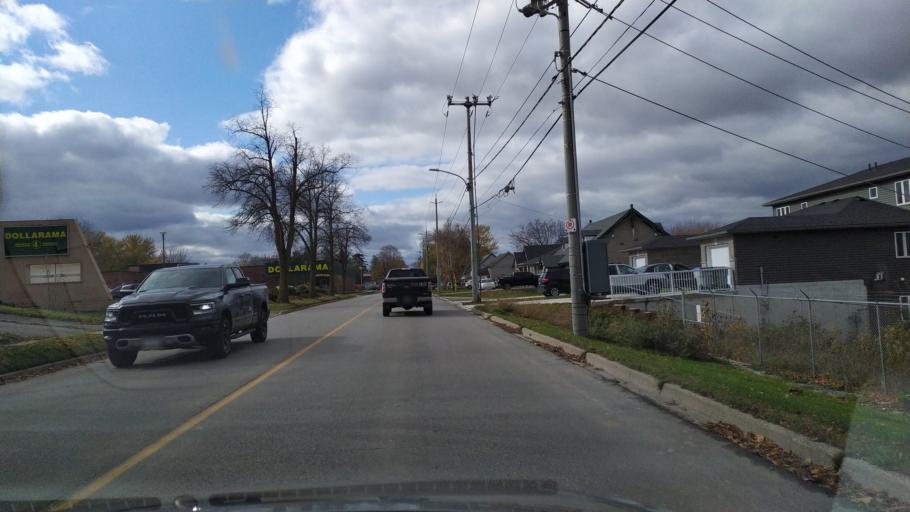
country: CA
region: Ontario
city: Stratford
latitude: 43.2615
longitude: -81.1235
